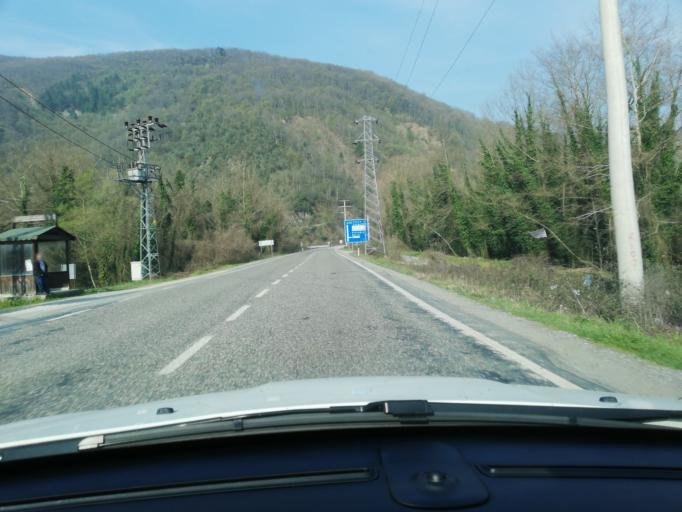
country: TR
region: Karabuk
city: Yenice
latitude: 41.2037
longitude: 32.3702
